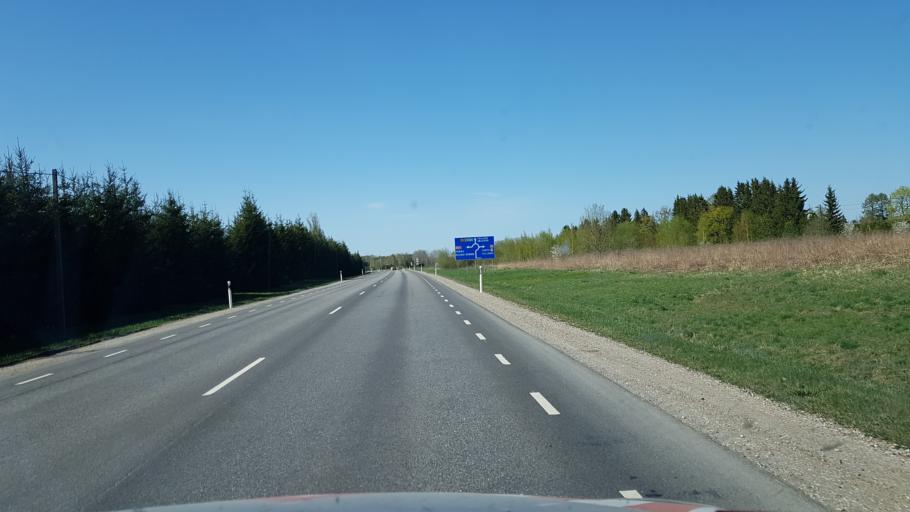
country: EE
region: Viljandimaa
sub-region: Viljandi linn
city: Viljandi
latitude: 58.3523
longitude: 25.5609
